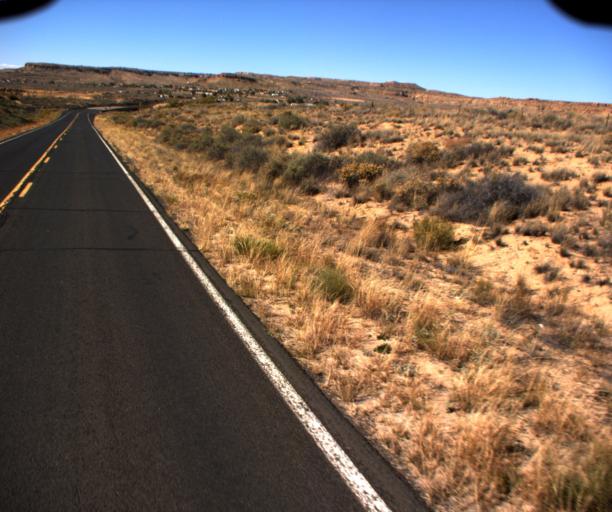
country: US
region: Arizona
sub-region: Navajo County
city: First Mesa
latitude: 35.8732
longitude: -110.5971
